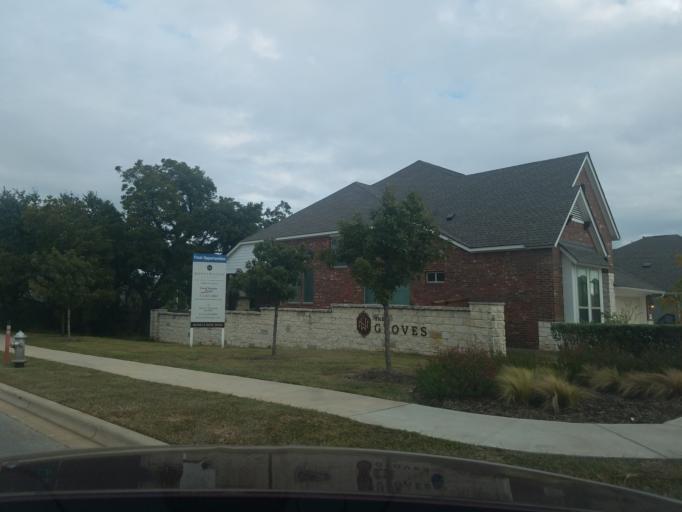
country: US
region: Texas
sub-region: Williamson County
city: Anderson Mill
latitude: 30.4830
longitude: -97.7900
